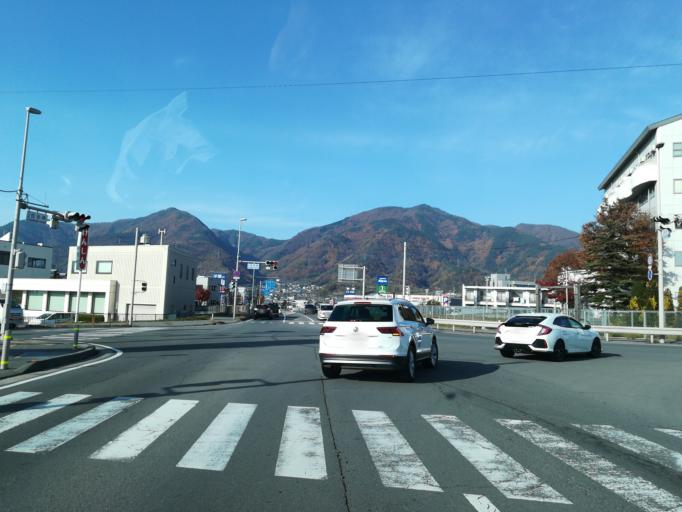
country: JP
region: Nagano
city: Ueda
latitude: 36.4018
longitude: 138.2737
